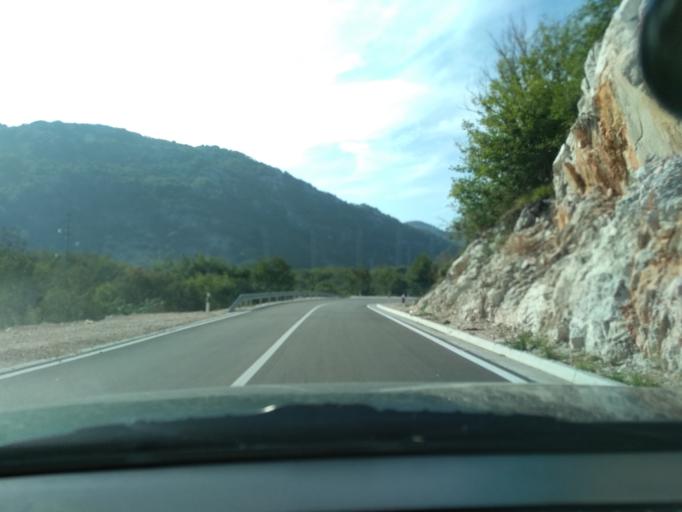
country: ME
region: Cetinje
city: Cetinje
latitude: 42.4279
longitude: 18.8659
